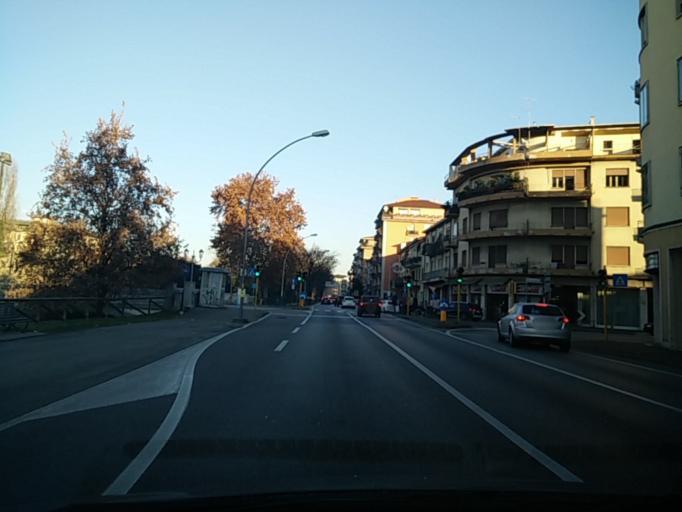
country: IT
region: Veneto
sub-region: Provincia di Treviso
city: Treviso
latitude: 45.6655
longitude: 12.2554
